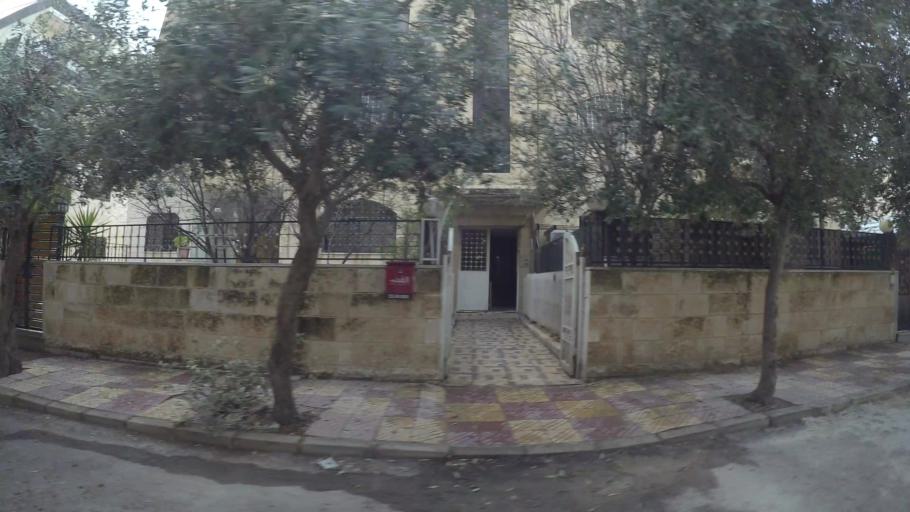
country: JO
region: Amman
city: Umm as Summaq
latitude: 31.8969
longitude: 35.8373
